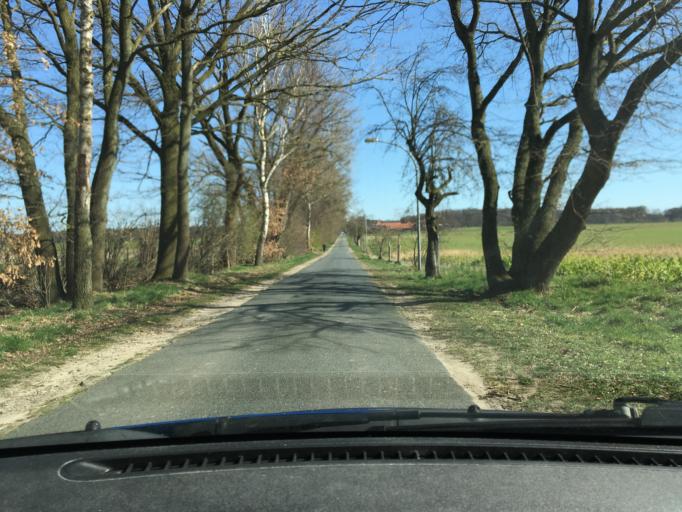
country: DE
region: Lower Saxony
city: Ebstorf
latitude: 53.0257
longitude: 10.4314
